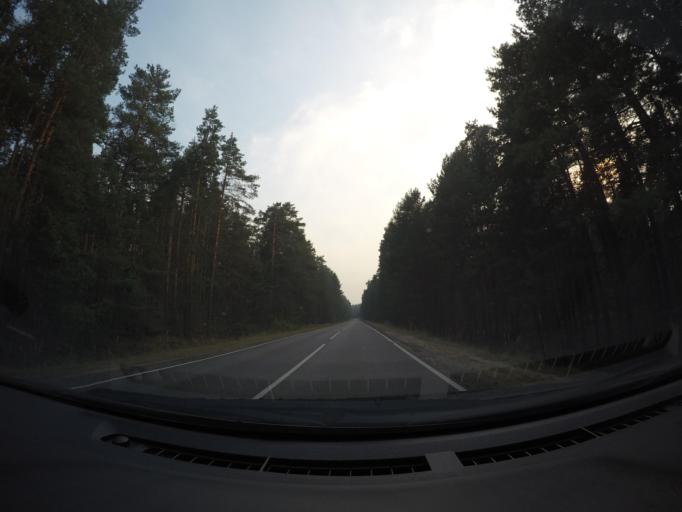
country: RU
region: Moskovskaya
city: Imeni Tsyurupy
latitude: 55.5131
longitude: 38.7215
